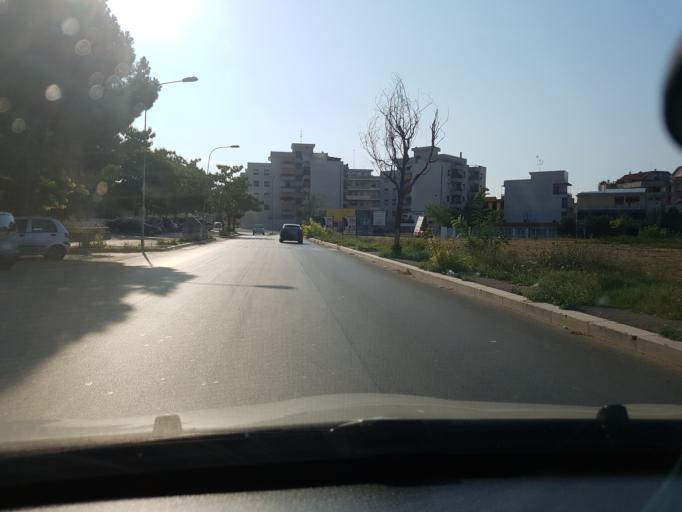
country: IT
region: Apulia
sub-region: Provincia di Foggia
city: Cerignola
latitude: 41.2662
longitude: 15.9076
